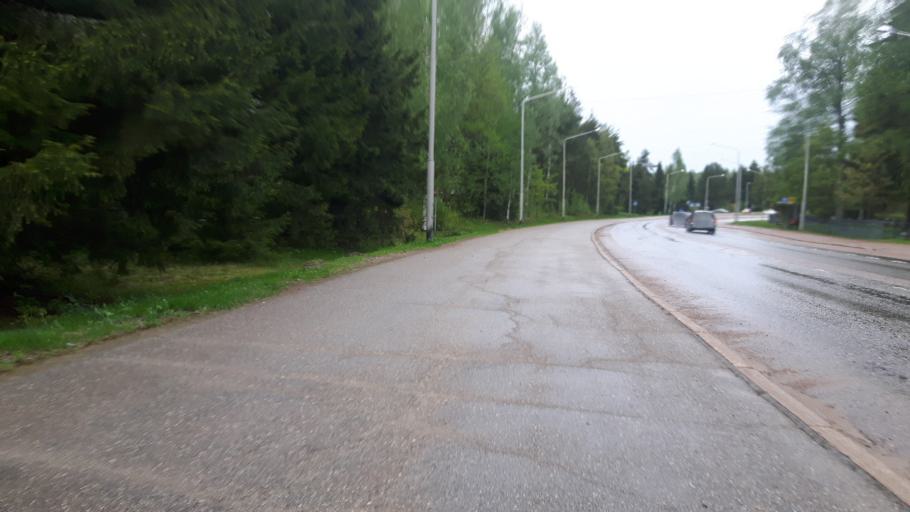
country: FI
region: Kymenlaakso
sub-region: Kotka-Hamina
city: Kotka
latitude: 60.4926
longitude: 26.8996
